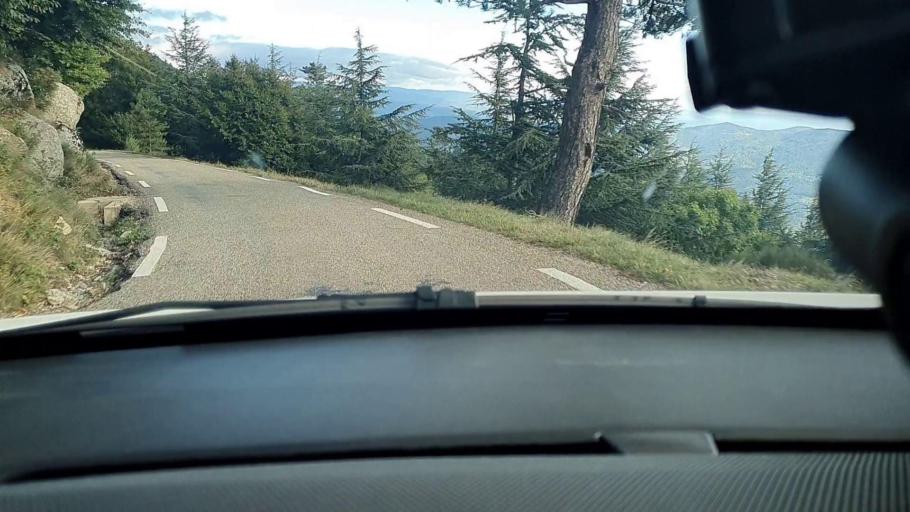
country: FR
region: Languedoc-Roussillon
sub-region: Departement du Gard
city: Branoux-les-Taillades
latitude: 44.3592
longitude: 3.9187
